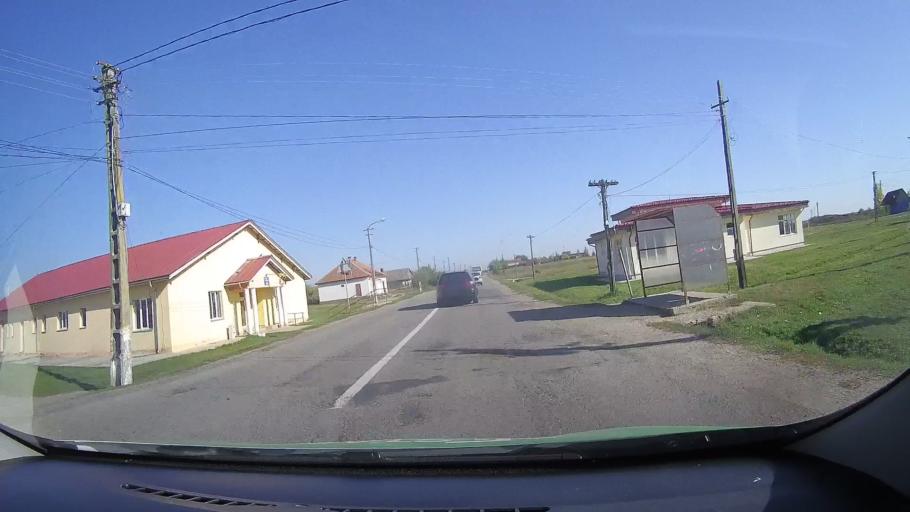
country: RO
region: Satu Mare
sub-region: Comuna Cauas
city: Cauas
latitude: 47.5699
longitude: 22.5451
